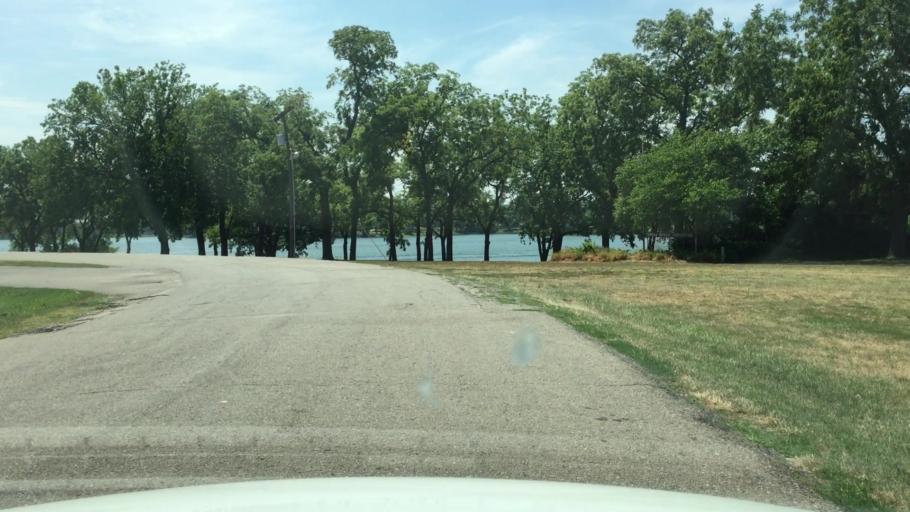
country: US
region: Kansas
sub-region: Shawnee County
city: Topeka
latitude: 39.0104
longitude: -95.6231
